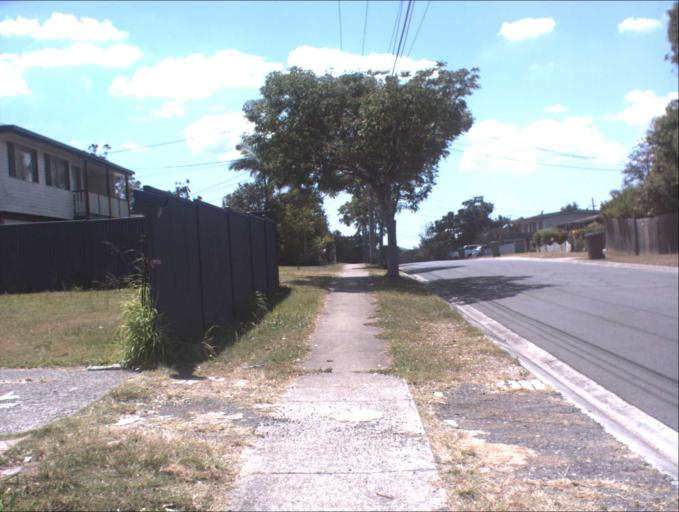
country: AU
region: Queensland
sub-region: Logan
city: Logan City
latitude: -27.6495
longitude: 153.1029
